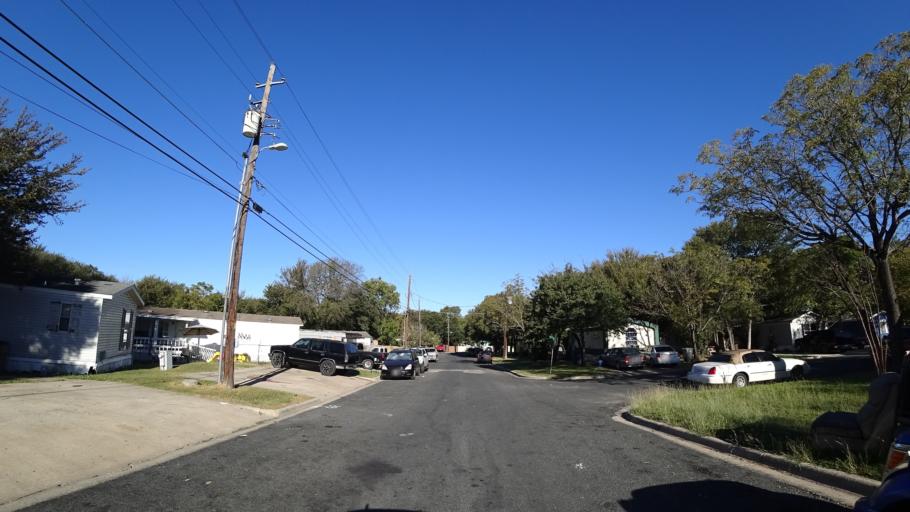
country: US
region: Texas
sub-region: Travis County
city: Austin
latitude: 30.2234
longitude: -97.6712
